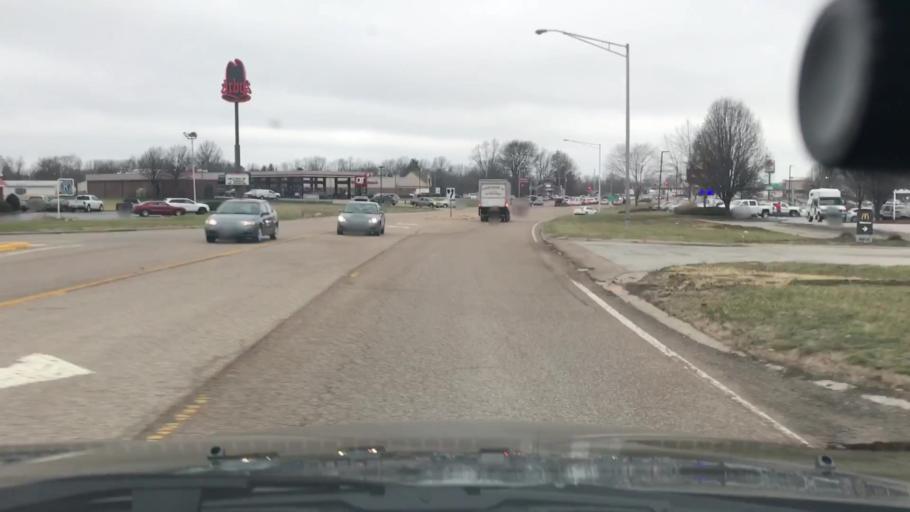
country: US
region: Illinois
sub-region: Madison County
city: Bethalto
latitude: 38.9007
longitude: -90.0564
